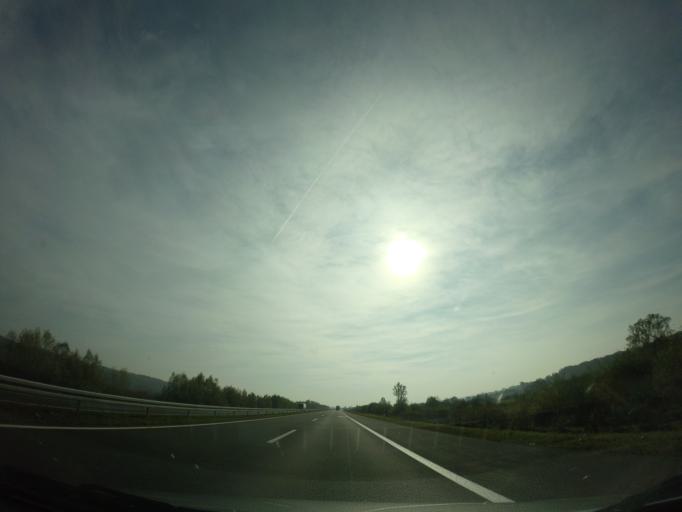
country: HR
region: Varazdinska
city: Remetinec
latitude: 46.0241
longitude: 16.2947
